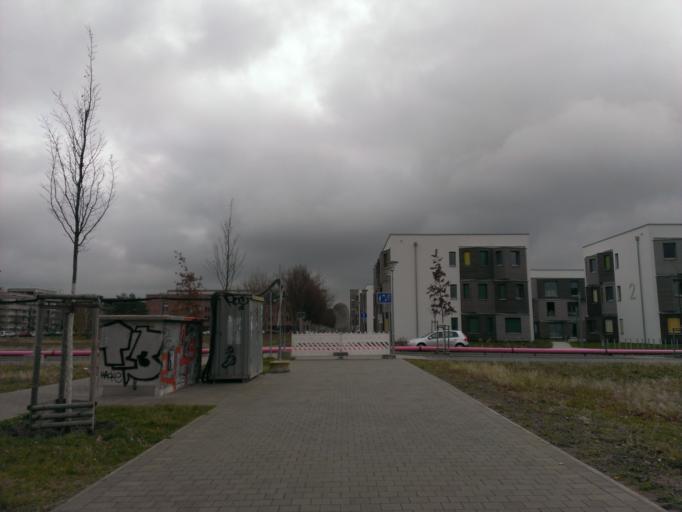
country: DE
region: Berlin
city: Adlershof
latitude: 52.4340
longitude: 13.5259
